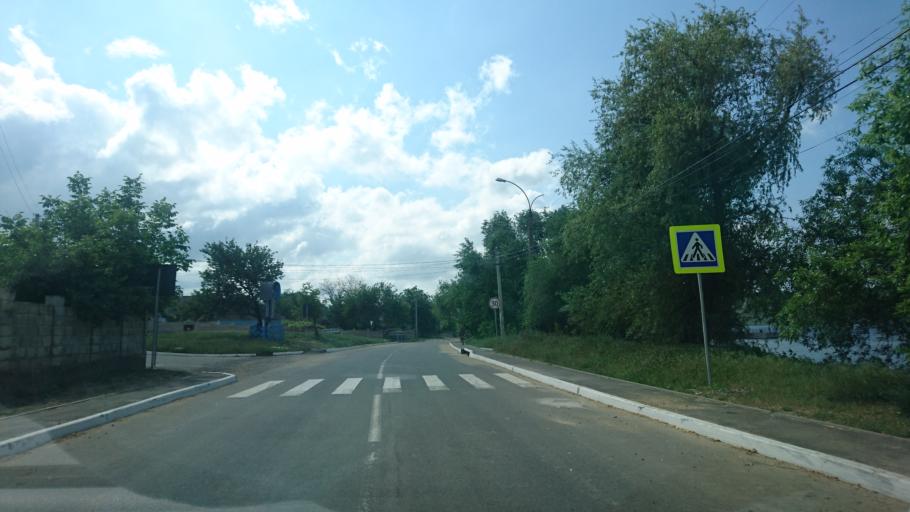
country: MD
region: Telenesti
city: Cocieri
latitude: 47.3526
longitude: 29.1072
